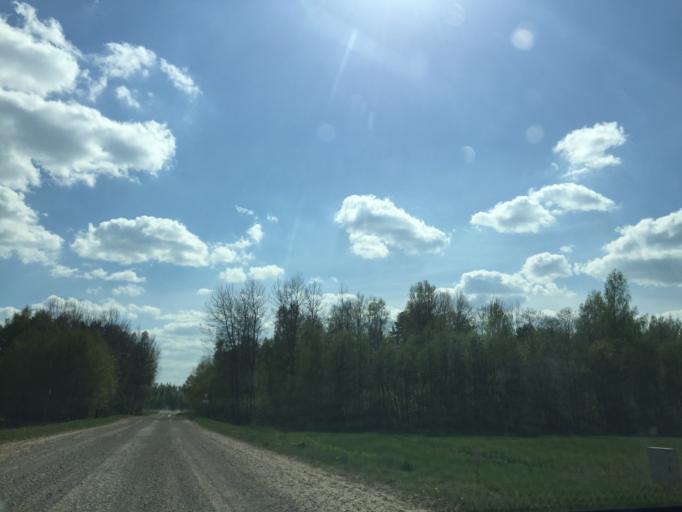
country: LV
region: Vecumnieki
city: Vecumnieki
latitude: 56.4259
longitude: 24.4976
